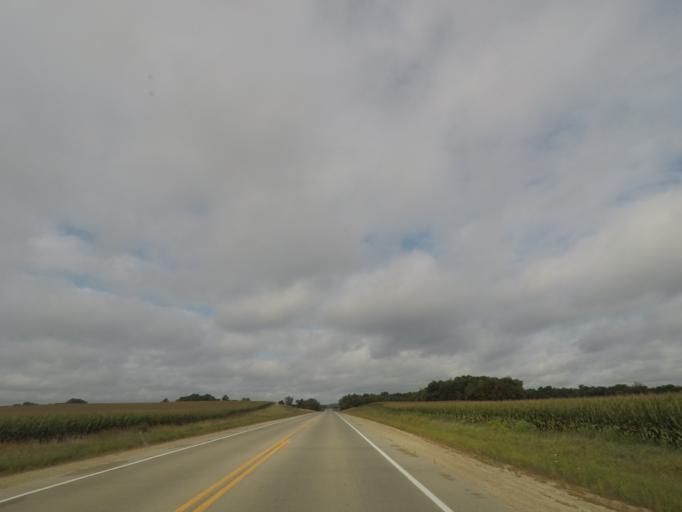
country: US
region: Wisconsin
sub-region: Jefferson County
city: Cambridge
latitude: 43.0195
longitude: -89.0455
